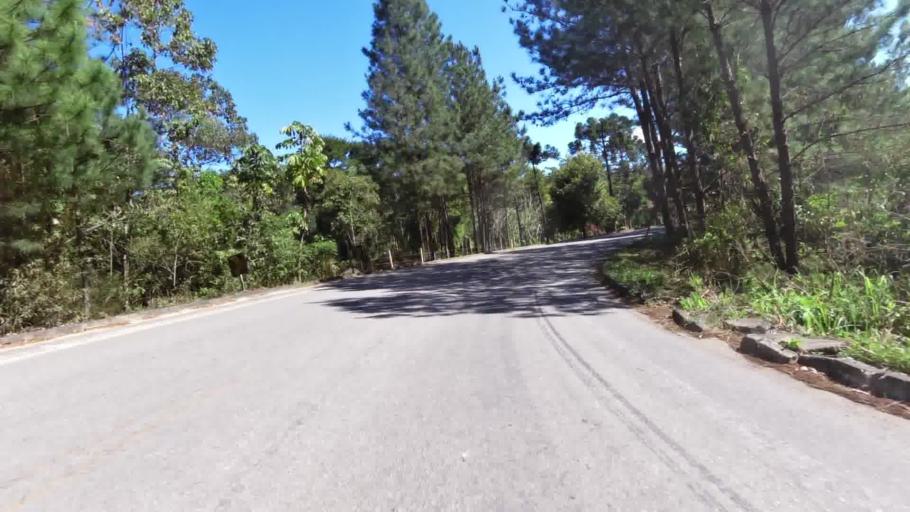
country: BR
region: Espirito Santo
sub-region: Vargem Alta
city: Vargem Alta
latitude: -20.6767
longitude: -40.9552
